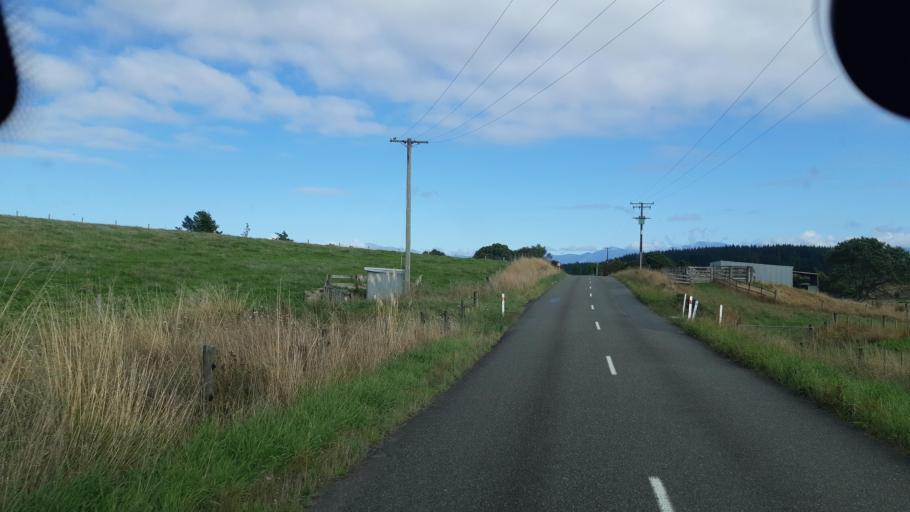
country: NZ
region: Tasman
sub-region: Tasman District
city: Mapua
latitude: -41.2429
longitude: 173.0431
